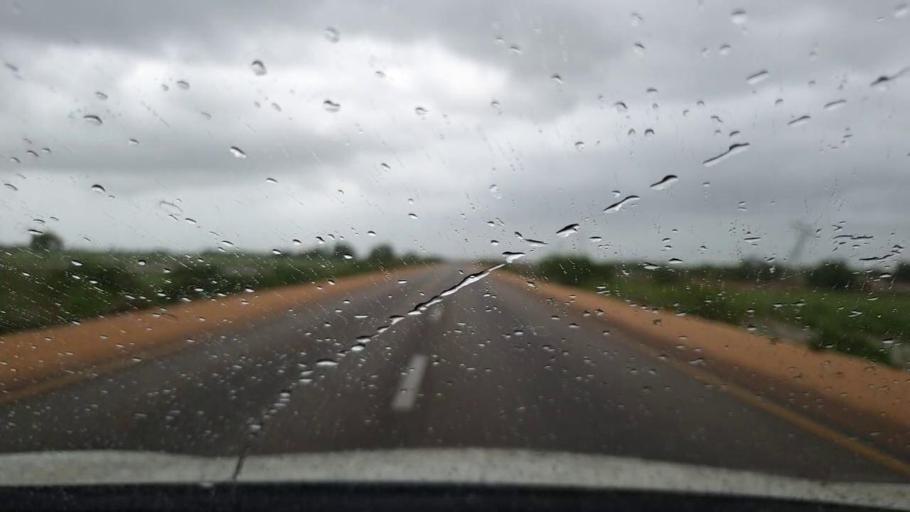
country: PK
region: Sindh
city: Badin
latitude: 24.6562
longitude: 68.6940
